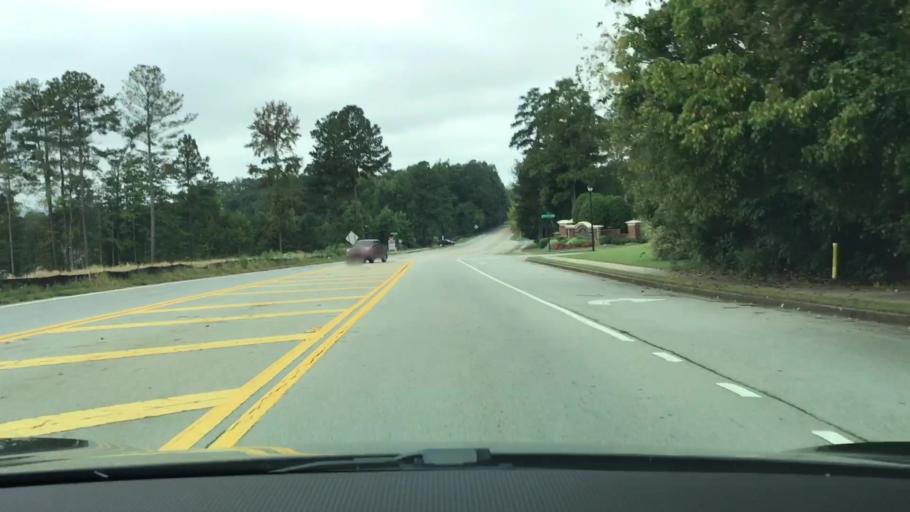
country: US
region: Georgia
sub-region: Barrow County
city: Auburn
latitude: 34.0718
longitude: -83.8487
